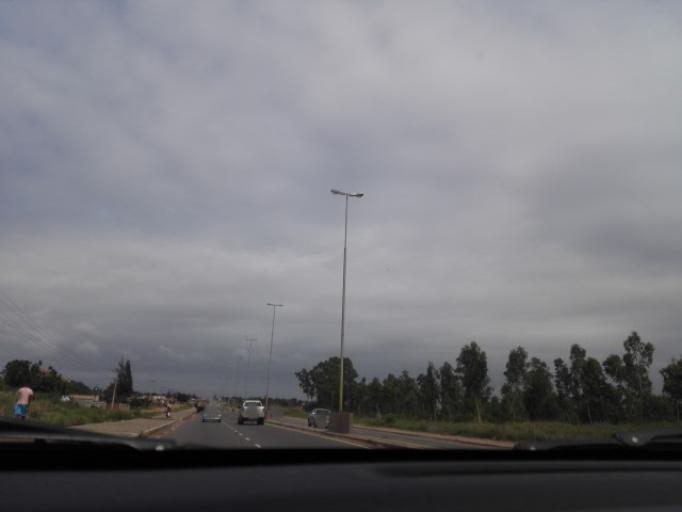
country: MZ
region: Maputo City
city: Maputo
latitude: -25.8291
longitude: 32.6102
